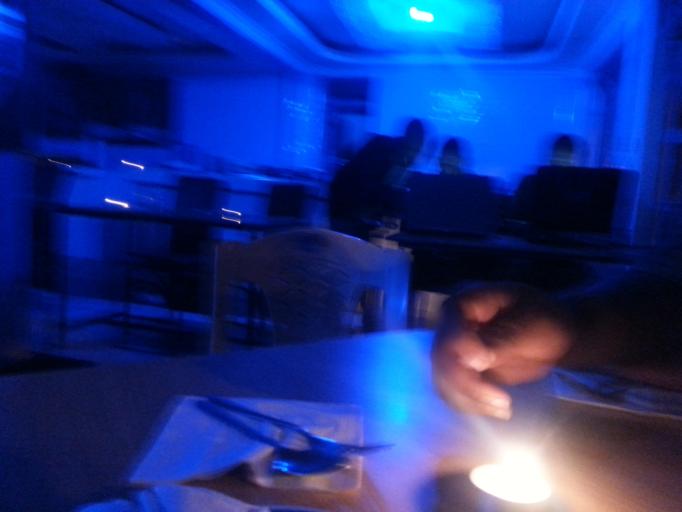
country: KE
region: Nairobi Area
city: Thika
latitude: -1.1065
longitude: 37.0147
